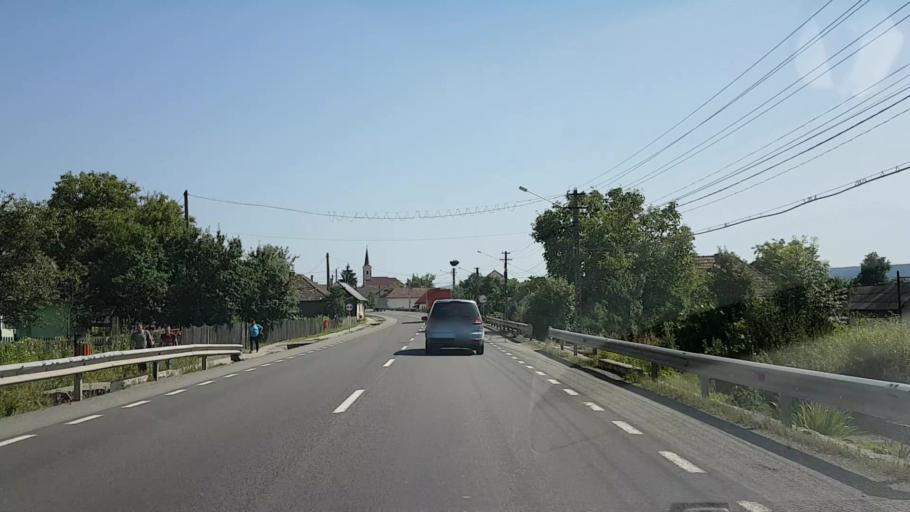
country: RO
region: Bistrita-Nasaud
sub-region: Comuna Sieu-Odorhei
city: Sieu-Odorhei
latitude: 47.1498
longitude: 24.3058
